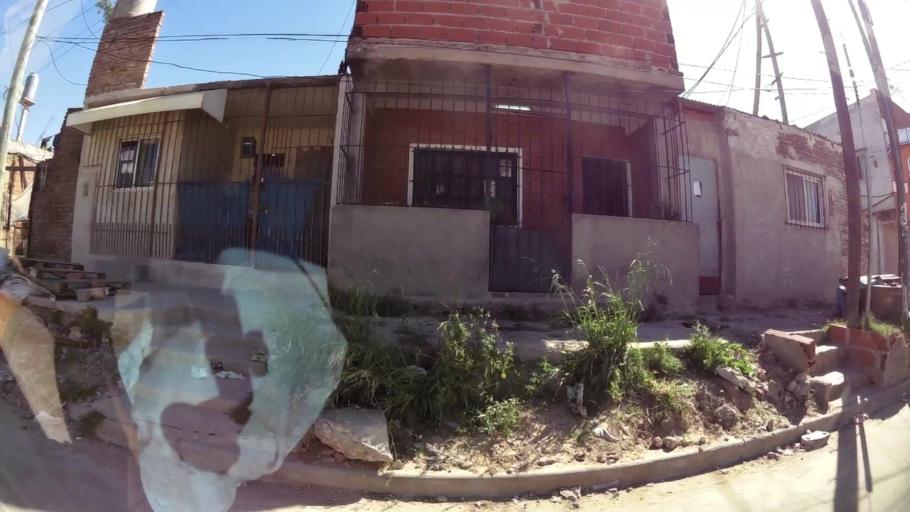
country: AR
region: Buenos Aires
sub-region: Partido de General San Martin
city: General San Martin
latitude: -34.5321
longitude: -58.5800
